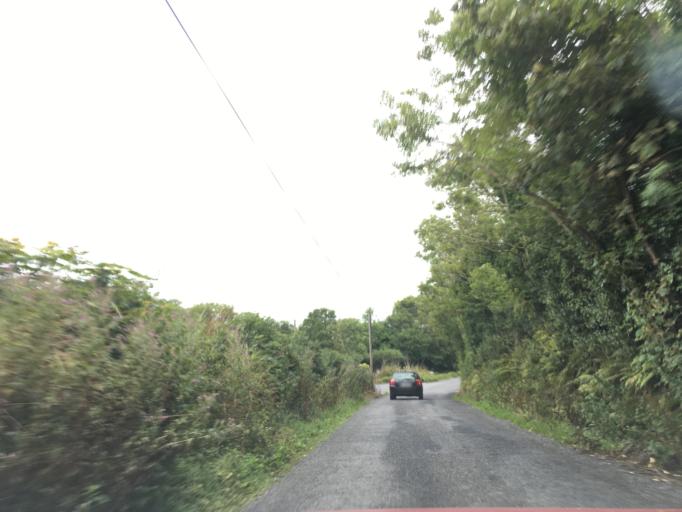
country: IE
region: Munster
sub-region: An Clar
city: Ennis
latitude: 52.7195
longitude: -9.0880
